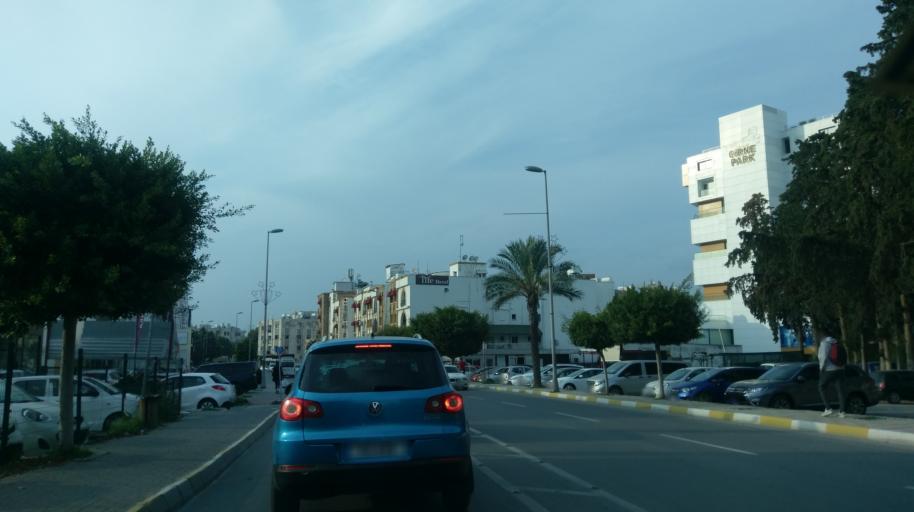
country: CY
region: Keryneia
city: Kyrenia
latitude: 35.3351
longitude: 33.3102
